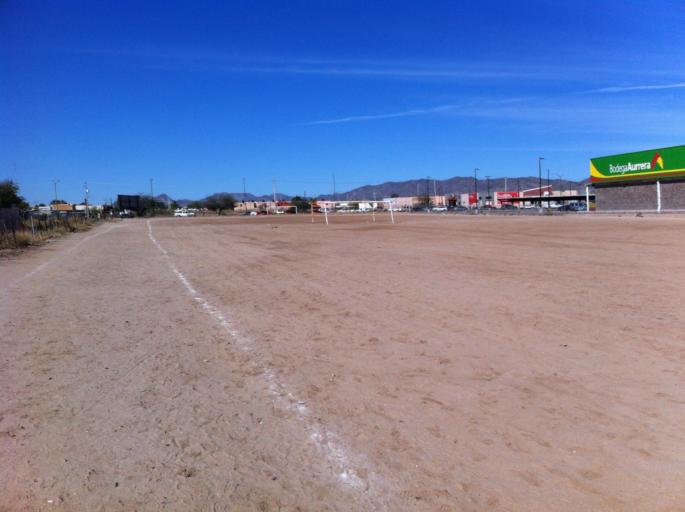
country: MX
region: Sonora
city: Hermosillo
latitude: 29.1149
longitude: -110.9999
